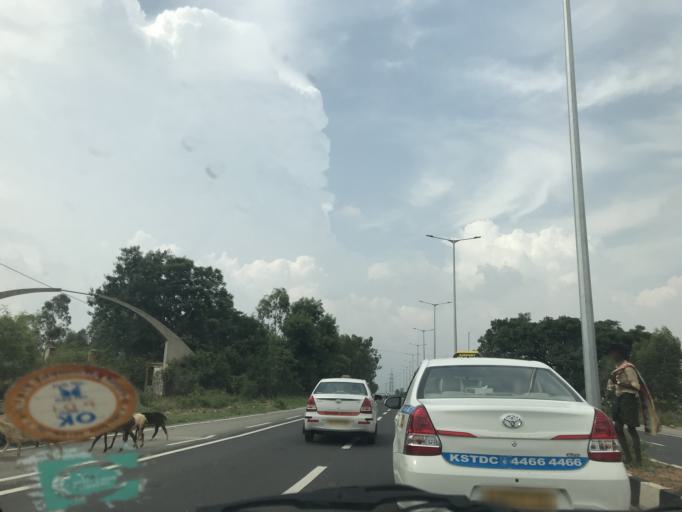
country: IN
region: Karnataka
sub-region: Bangalore Rural
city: Devanhalli
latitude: 13.1605
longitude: 77.6842
